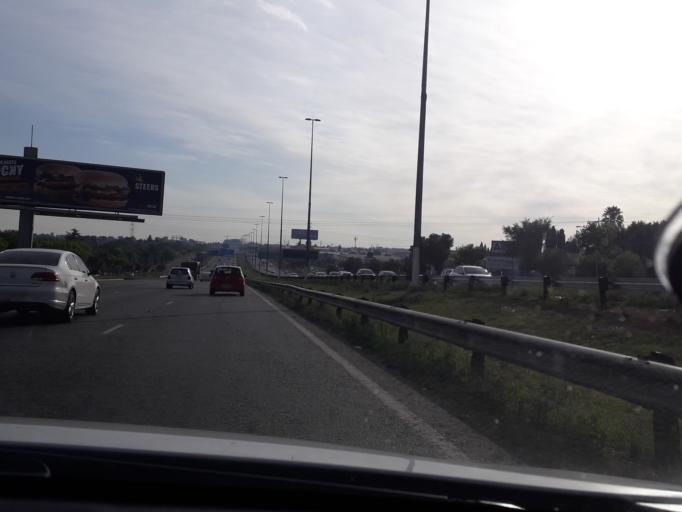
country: ZA
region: Gauteng
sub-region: City of Johannesburg Metropolitan Municipality
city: Modderfontein
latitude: -26.1494
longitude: 28.1739
